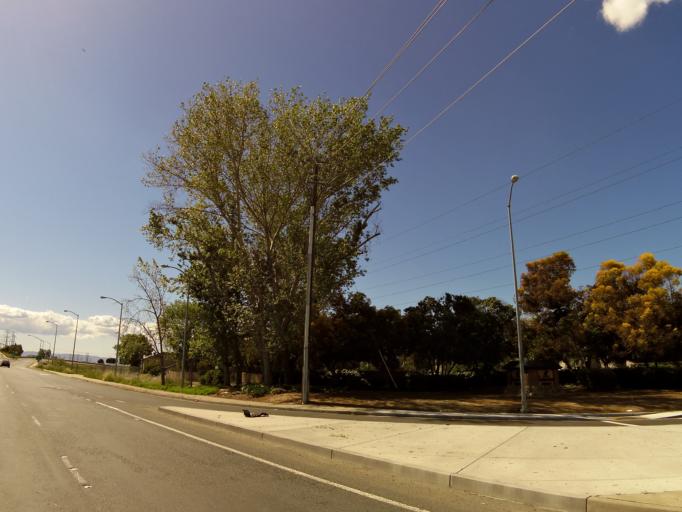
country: US
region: California
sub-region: Alameda County
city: Fremont
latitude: 37.5093
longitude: -121.9631
